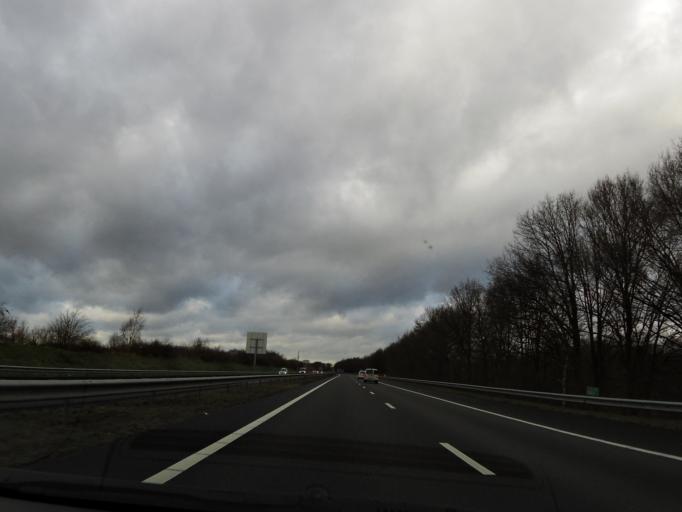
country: NL
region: Limburg
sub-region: Gemeente Peel en Maas
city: Maasbree
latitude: 51.4592
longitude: 6.0617
